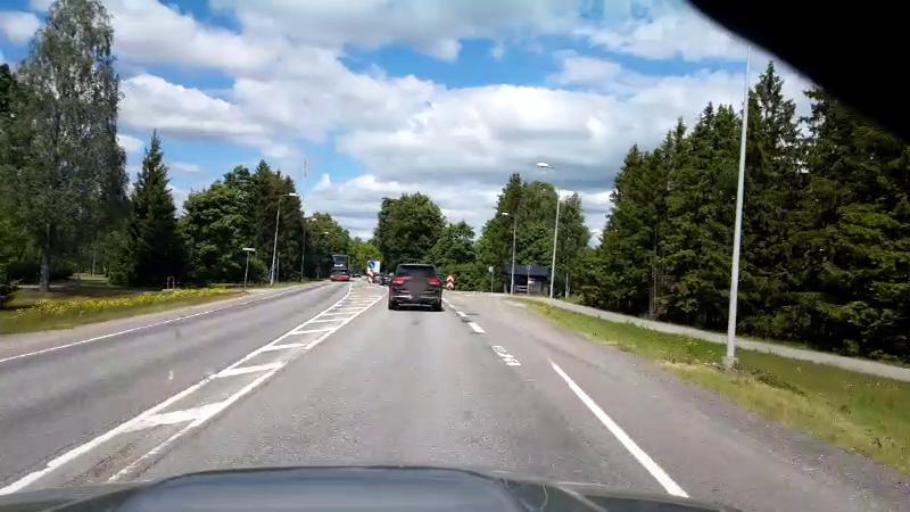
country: EE
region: Harju
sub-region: Keila linn
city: Keila
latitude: 59.1345
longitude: 24.4995
